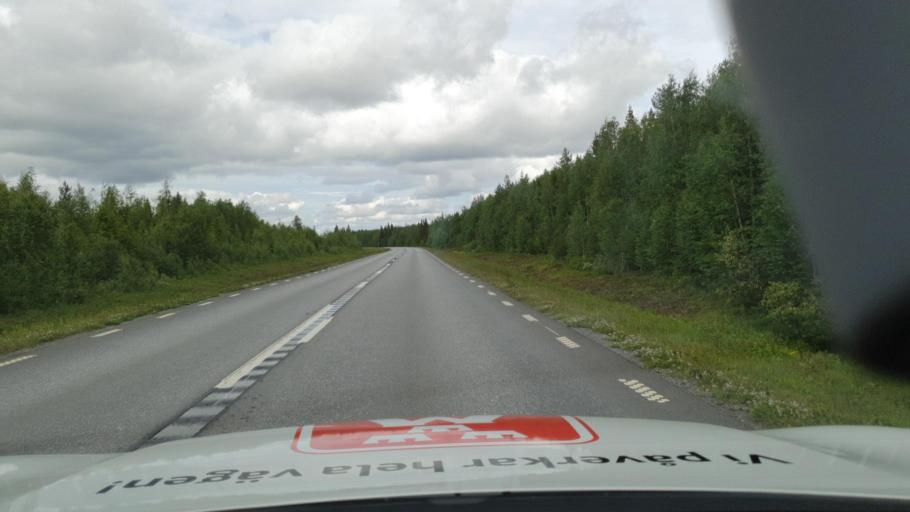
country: SE
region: Vaesterbotten
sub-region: Vilhelmina Kommun
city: Vilhelmina
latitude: 64.3653
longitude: 16.7095
